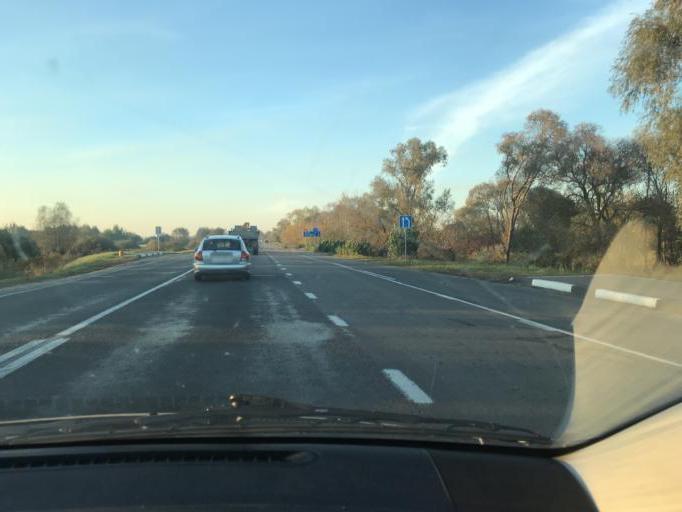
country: BY
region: Brest
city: Pinsk
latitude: 52.0745
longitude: 26.1487
